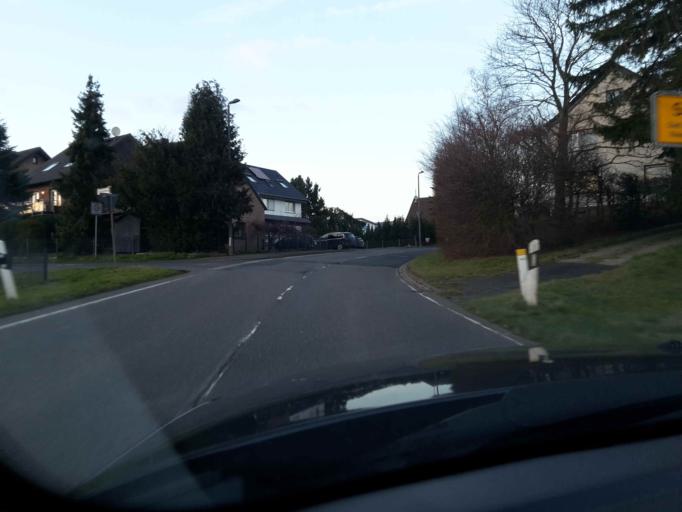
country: DE
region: North Rhine-Westphalia
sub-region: Regierungsbezirk Koln
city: Hennef
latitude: 50.7116
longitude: 7.3139
